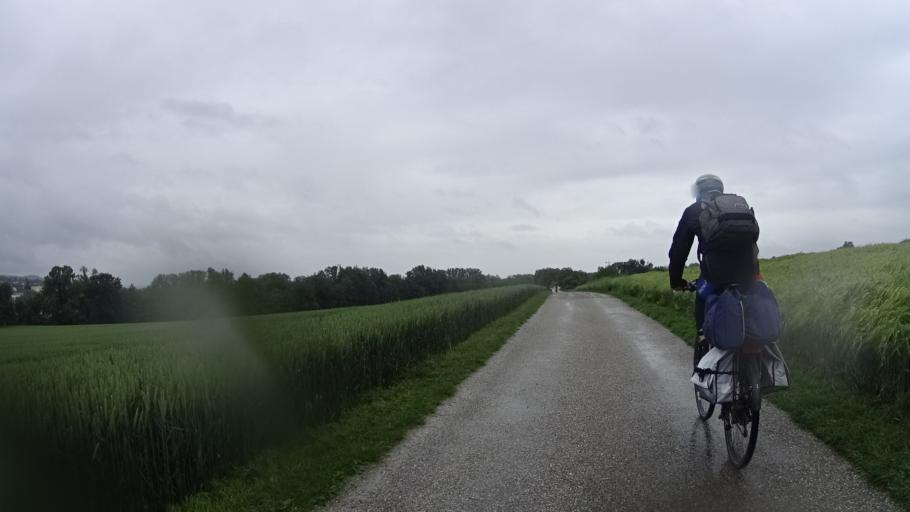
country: AT
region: Upper Austria
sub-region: Politischer Bezirk Scharding
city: Scharding
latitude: 48.4772
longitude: 13.4324
